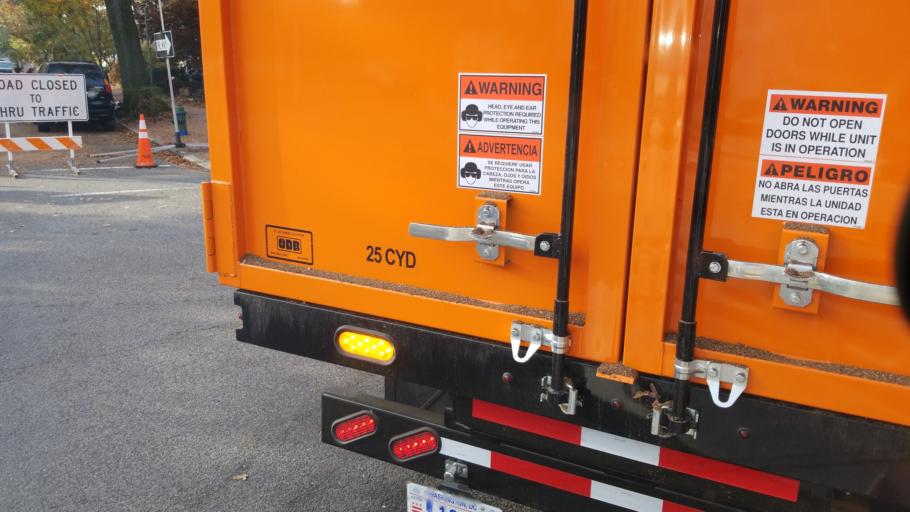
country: US
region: Washington, D.C.
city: Washington, D.C.
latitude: 38.8908
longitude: -76.9959
